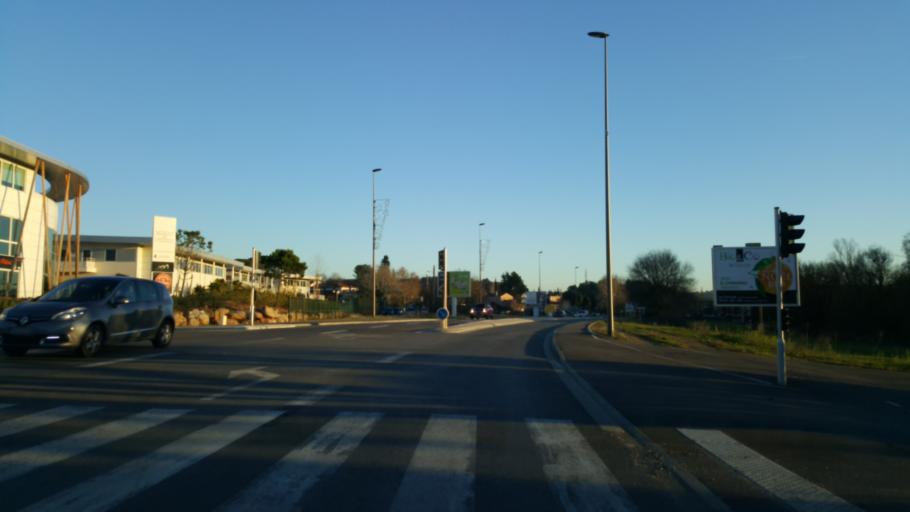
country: FR
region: Provence-Alpes-Cote d'Azur
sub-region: Departement des Bouches-du-Rhone
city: Meyreuil
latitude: 43.4961
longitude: 5.5215
